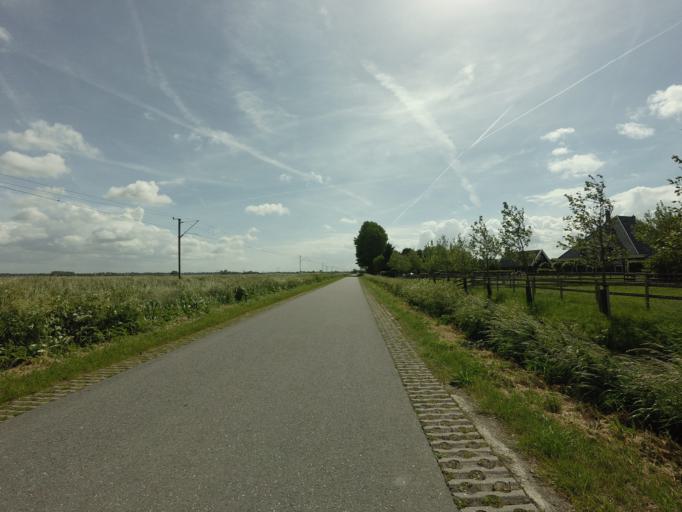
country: NL
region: North Holland
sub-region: Gemeente Opmeer
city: Opmeer
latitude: 52.6595
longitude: 4.9807
